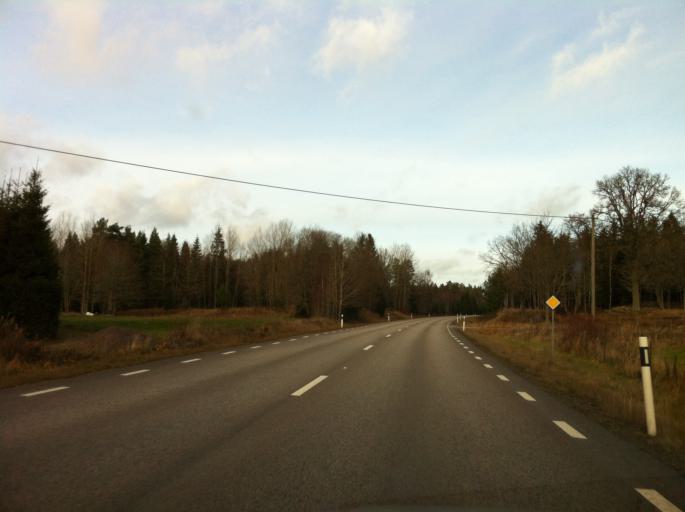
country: SE
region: Kronoberg
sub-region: Uppvidinge Kommun
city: Aseda
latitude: 57.1636
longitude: 15.3620
